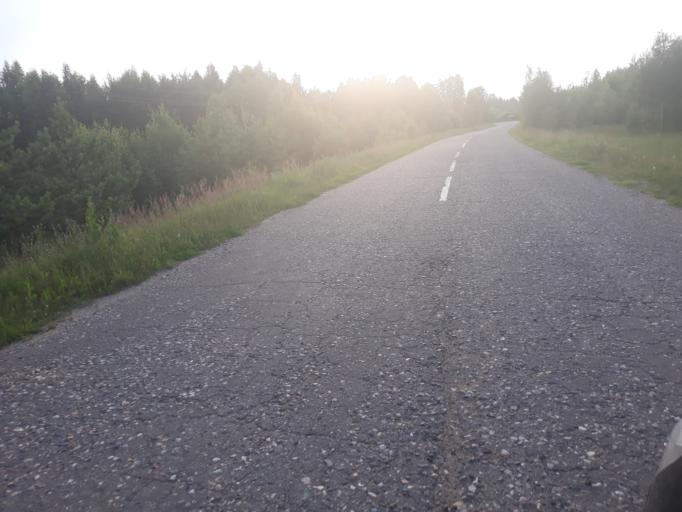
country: RU
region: Jaroslavl
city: Petrovsk
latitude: 56.8750
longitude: 39.0826
